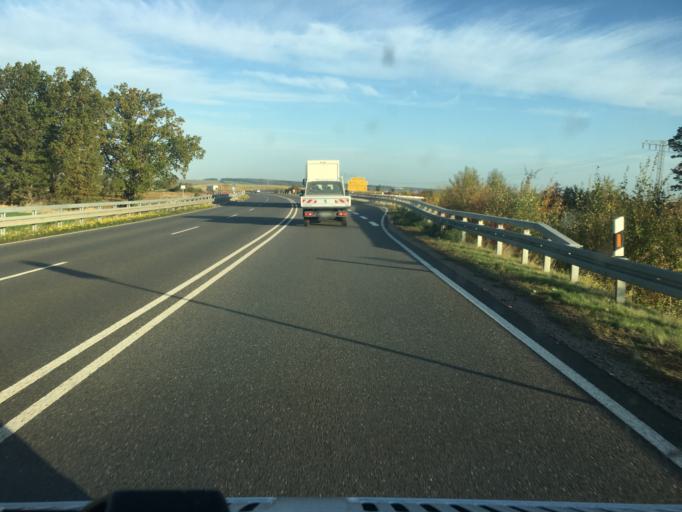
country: DE
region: Saxony
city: Lichtentanne
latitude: 50.6811
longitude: 12.4473
